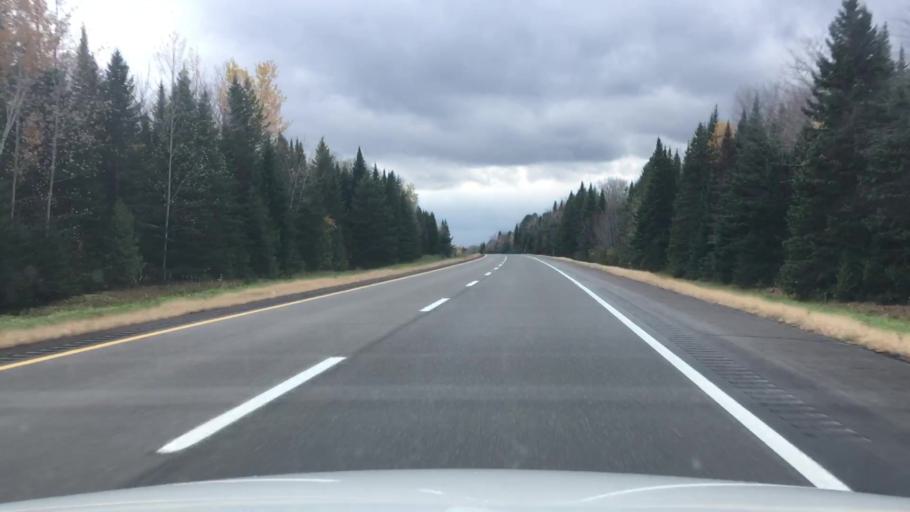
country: US
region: Maine
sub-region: Penobscot County
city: Patten
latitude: 46.0914
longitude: -68.2009
